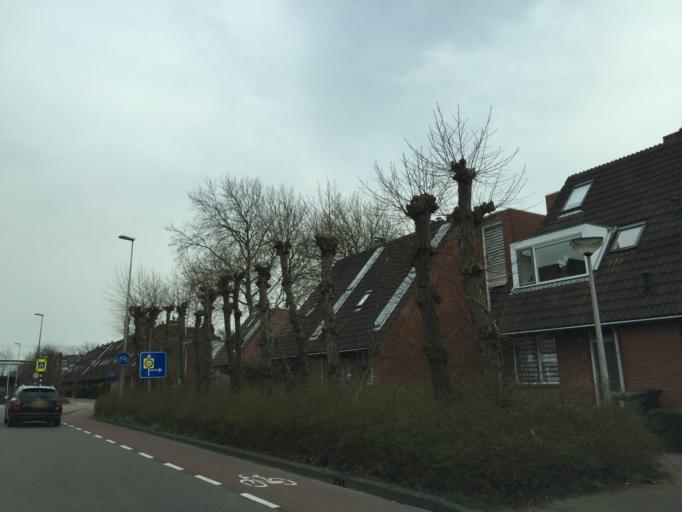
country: NL
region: South Holland
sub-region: Gemeente Zoetermeer
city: Zoetermeer
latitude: 52.0640
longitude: 4.5138
